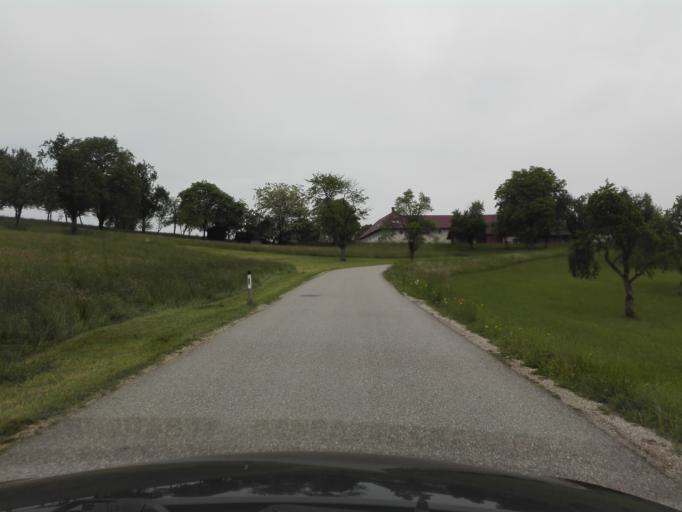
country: AT
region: Upper Austria
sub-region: Politischer Bezirk Gmunden
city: Scharnstein
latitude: 47.9208
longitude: 13.9718
